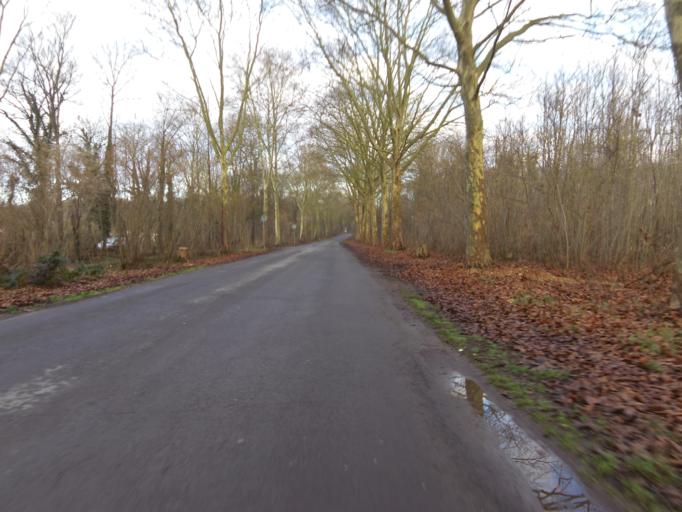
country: DE
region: Rheinland-Pfalz
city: Worms
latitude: 49.6178
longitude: 8.3785
